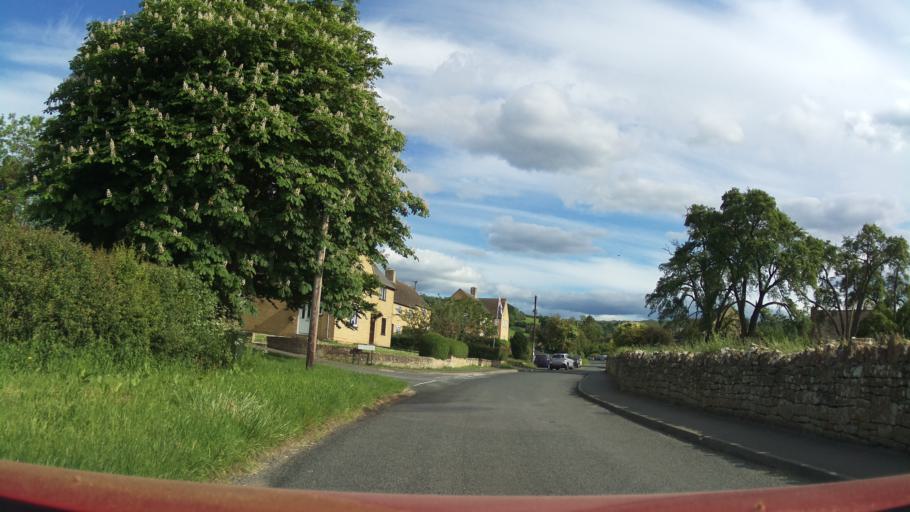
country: GB
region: England
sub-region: Gloucestershire
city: Chipping Campden
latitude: 52.0679
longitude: -1.8163
